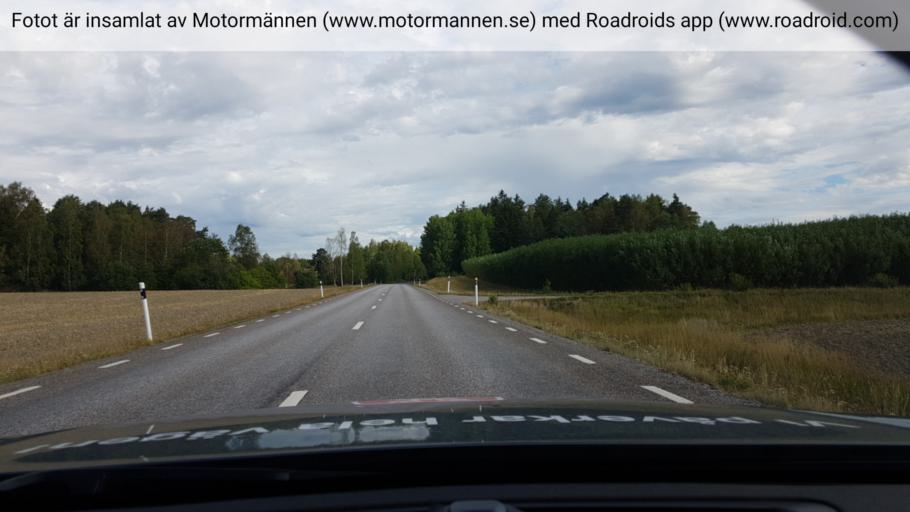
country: SE
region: Uppsala
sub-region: Heby Kommun
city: Morgongava
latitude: 59.8407
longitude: 16.9256
